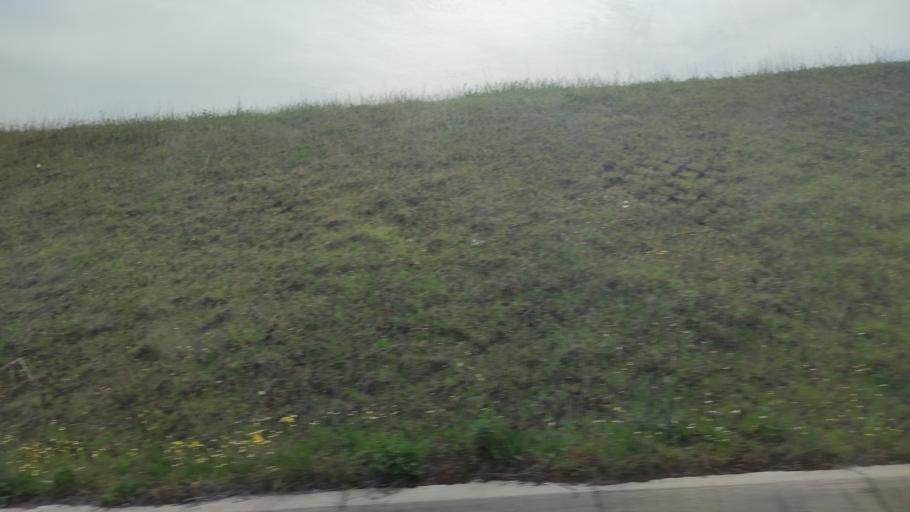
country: RO
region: Constanta
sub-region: Oras Murfatlar
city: Siminoc
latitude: 44.1434
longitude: 28.3594
